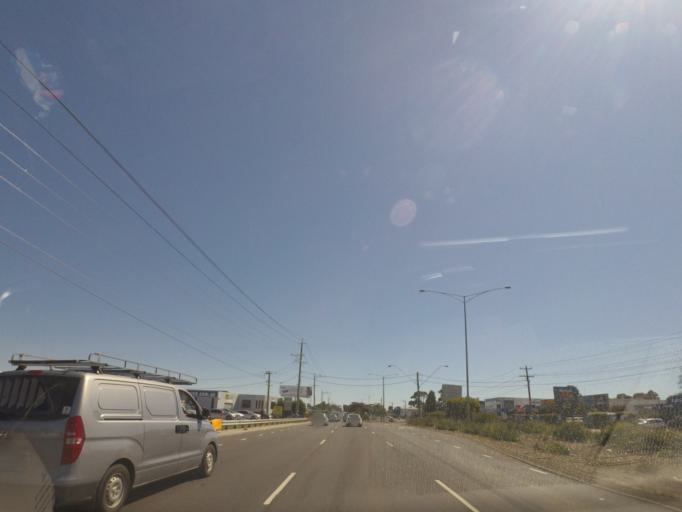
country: AU
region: Victoria
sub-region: Hume
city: Campbellfield
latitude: -37.6858
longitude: 144.9575
